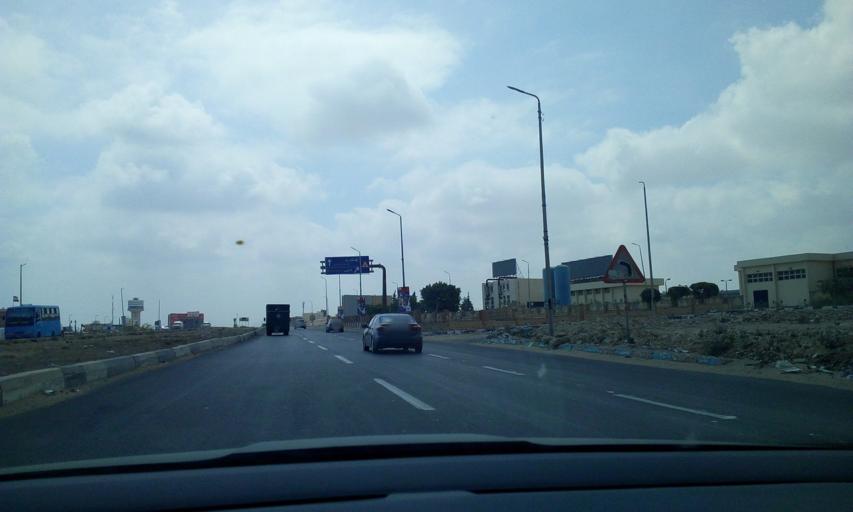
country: EG
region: Muhafazat Matruh
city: Al `Alamayn
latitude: 30.8372
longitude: 28.9562
